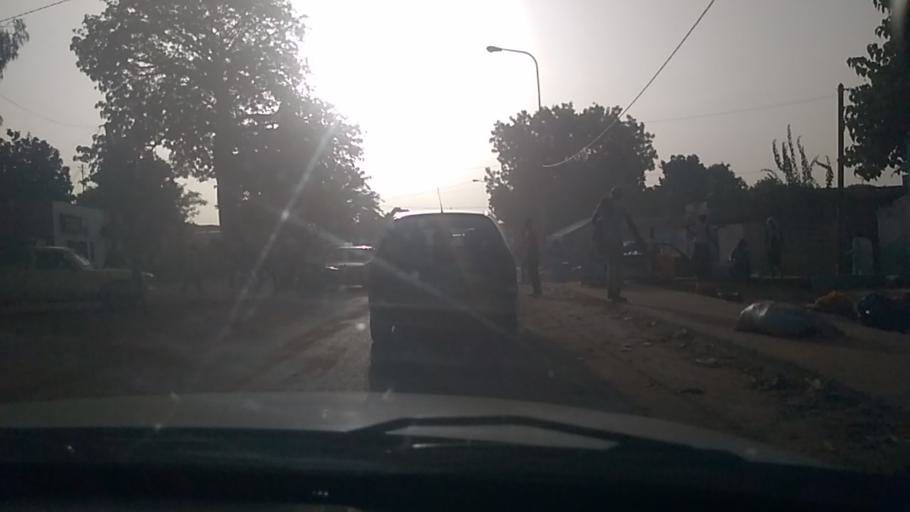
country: SN
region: Thies
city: Thies Nones
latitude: 14.7859
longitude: -16.9203
